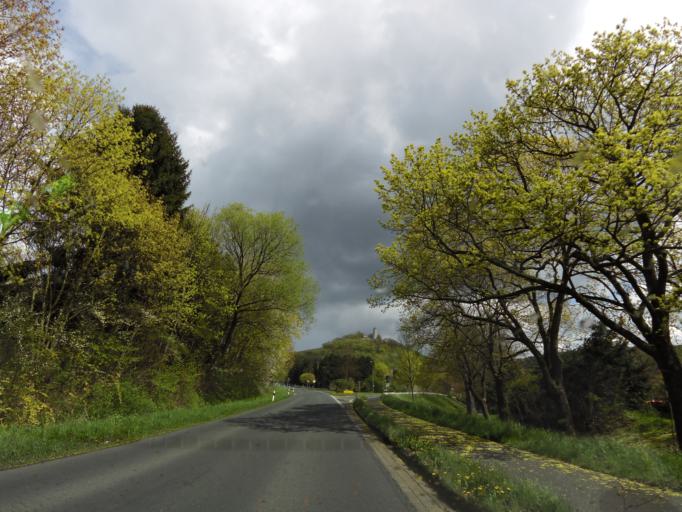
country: DE
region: Lower Saxony
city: Bovenden
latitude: 51.5971
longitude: 9.9547
